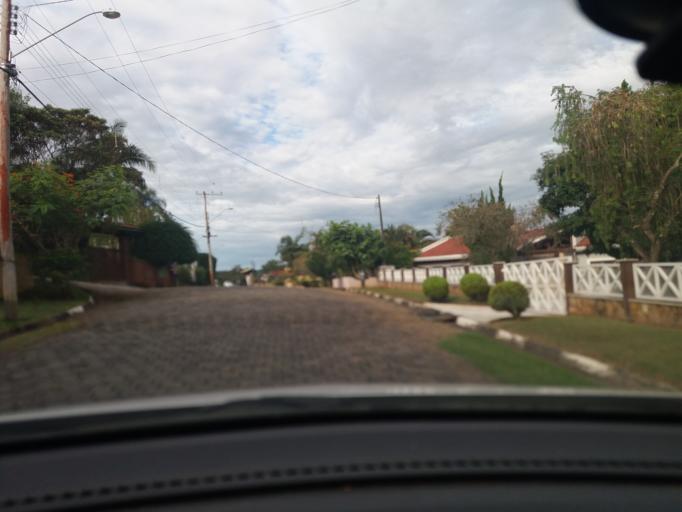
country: BR
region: Sao Paulo
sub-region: Bom Jesus Dos Perdoes
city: Bom Jesus dos Perdoes
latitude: -23.1687
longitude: -46.4537
